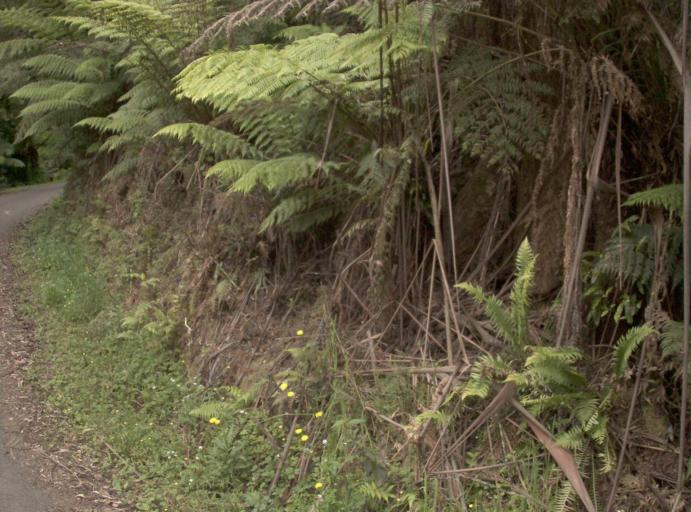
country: AU
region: Victoria
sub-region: Latrobe
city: Traralgon
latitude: -38.4529
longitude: 146.5403
